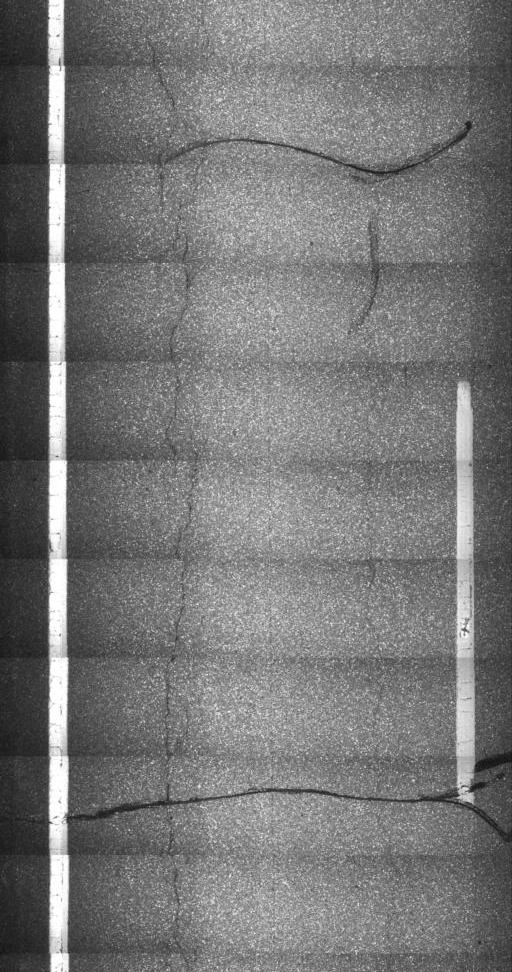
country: US
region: Vermont
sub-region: Windsor County
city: Woodstock
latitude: 43.7552
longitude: -72.4502
